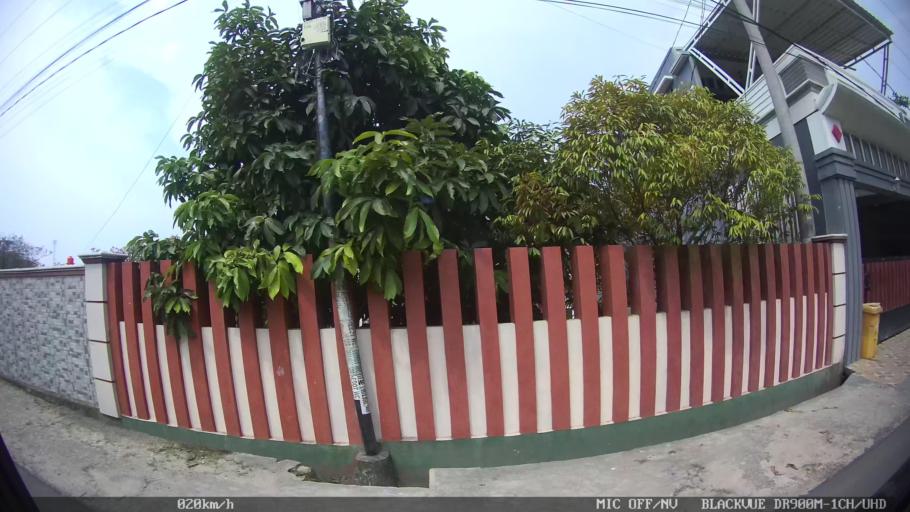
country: ID
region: Lampung
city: Bandarlampung
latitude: -5.4256
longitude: 105.2833
